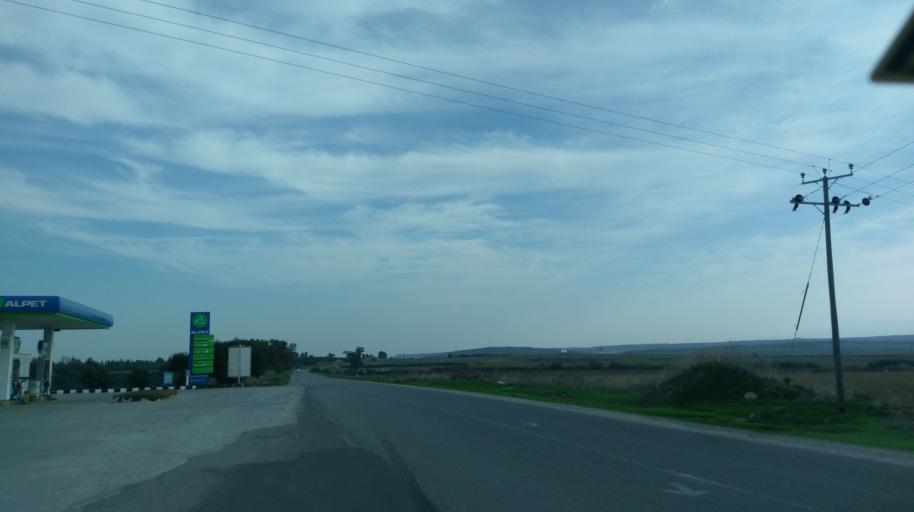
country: CY
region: Lefkosia
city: Mammari
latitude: 35.2254
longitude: 33.1733
